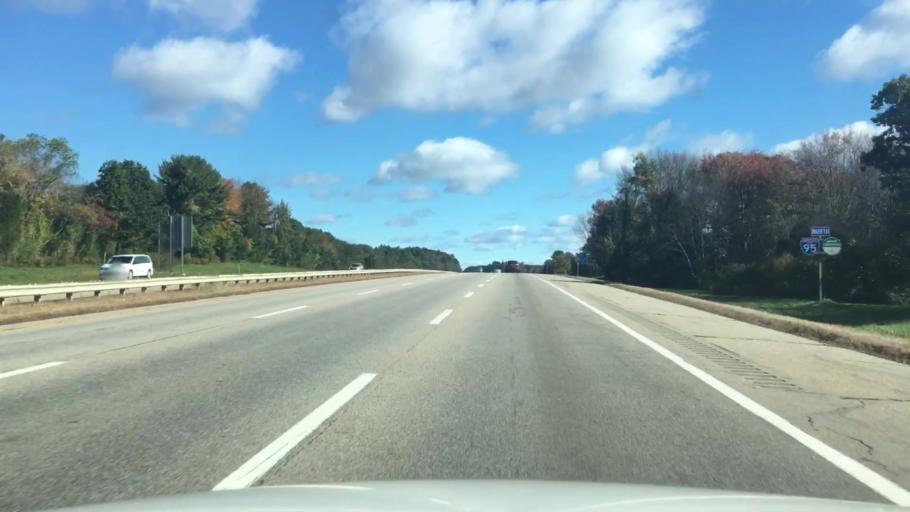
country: US
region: Maine
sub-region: York County
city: Kittery
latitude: 43.1162
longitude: -70.7324
